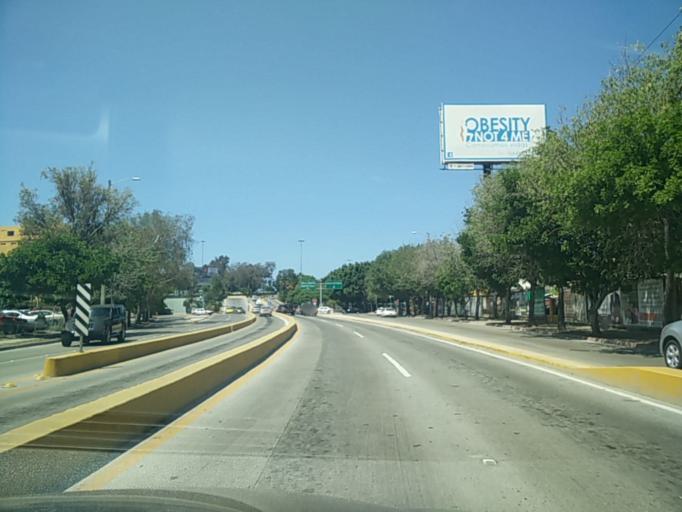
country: MX
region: Baja California
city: Tijuana
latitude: 32.5385
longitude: -117.0232
